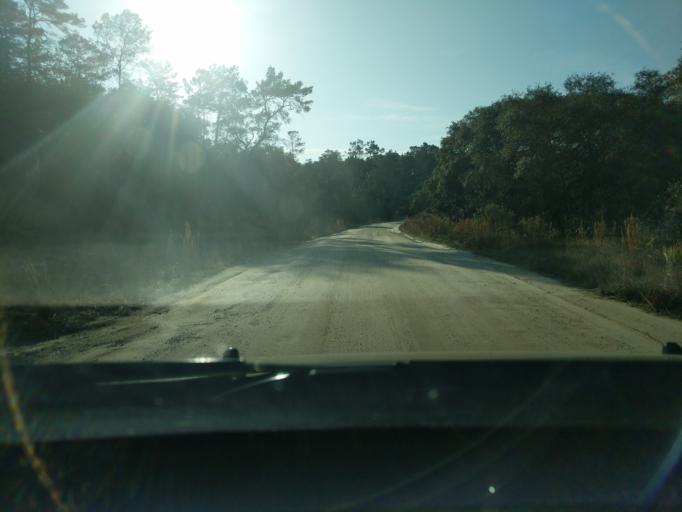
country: US
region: Florida
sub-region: Marion County
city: Silver Springs Shores
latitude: 29.2170
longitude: -81.8242
